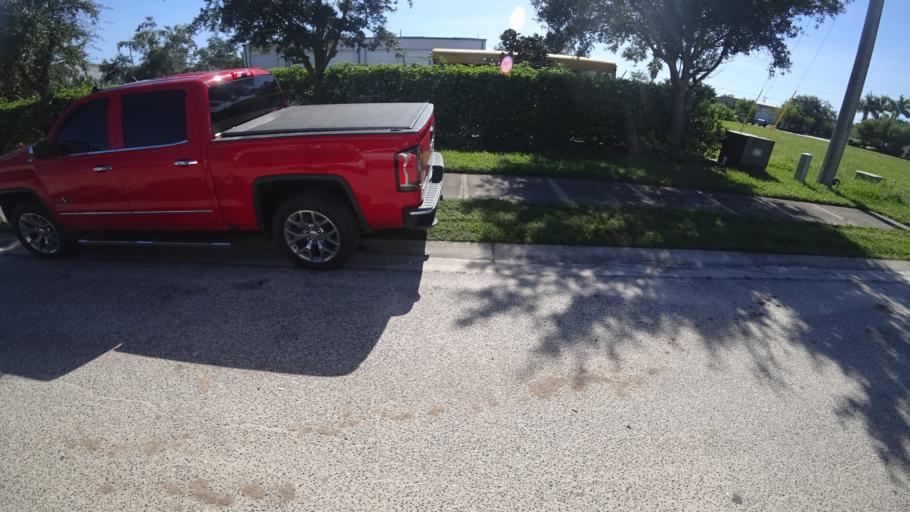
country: US
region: Florida
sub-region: Manatee County
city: Whitfield
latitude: 27.4124
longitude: -82.5399
